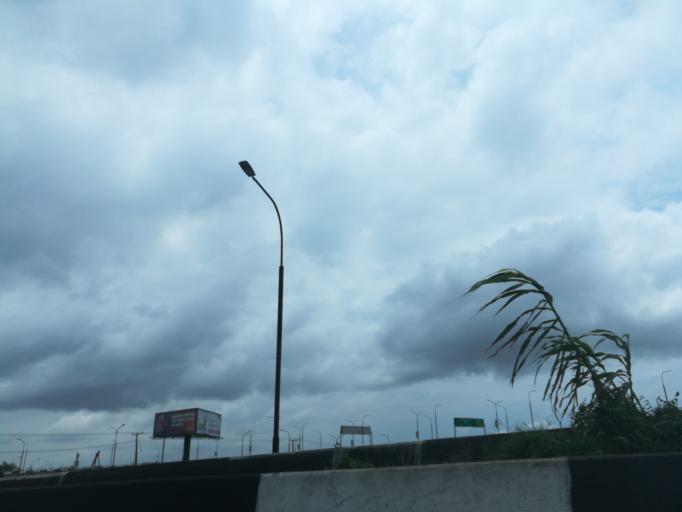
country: NG
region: Lagos
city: Lagos
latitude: 6.4567
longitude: 3.4065
